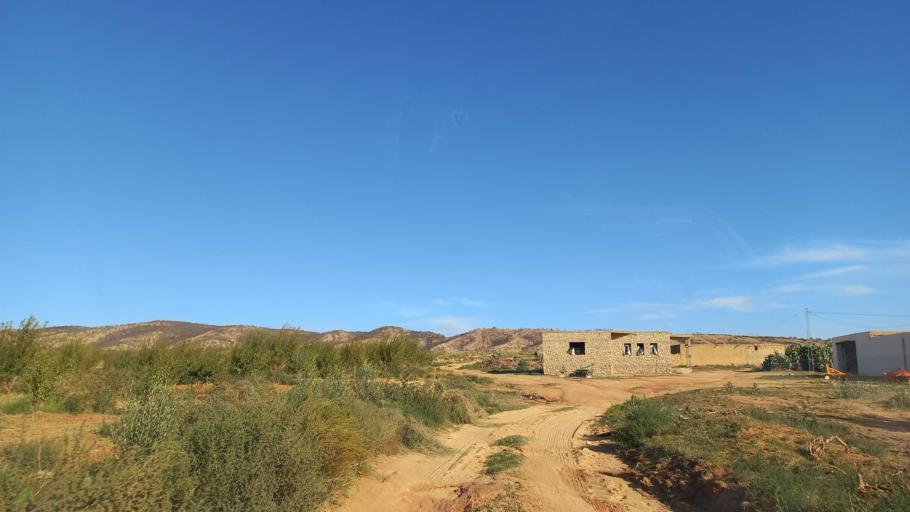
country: TN
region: Al Qasrayn
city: Sbiba
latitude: 35.3346
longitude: 9.1284
